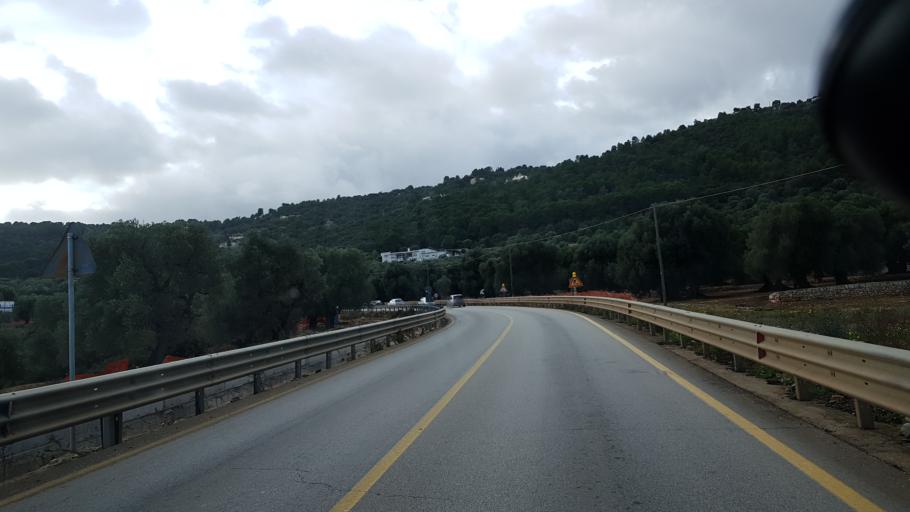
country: IT
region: Apulia
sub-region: Provincia di Brindisi
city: Lamie di Olimpie-Selva
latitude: 40.8215
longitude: 17.3468
